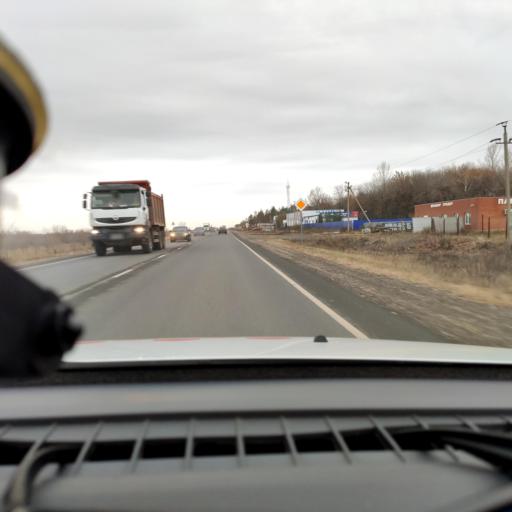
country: RU
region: Samara
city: Samara
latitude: 53.1238
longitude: 50.1893
